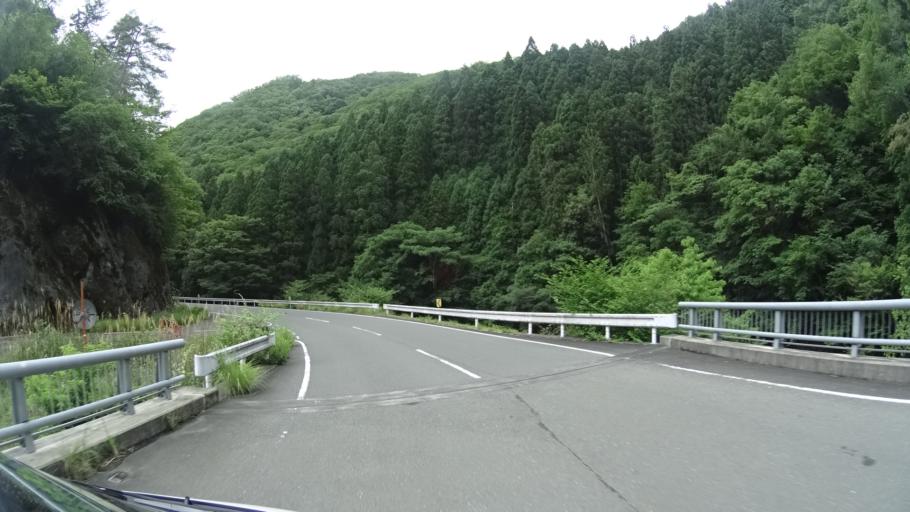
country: JP
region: Hyogo
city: Sasayama
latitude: 35.0626
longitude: 135.3947
